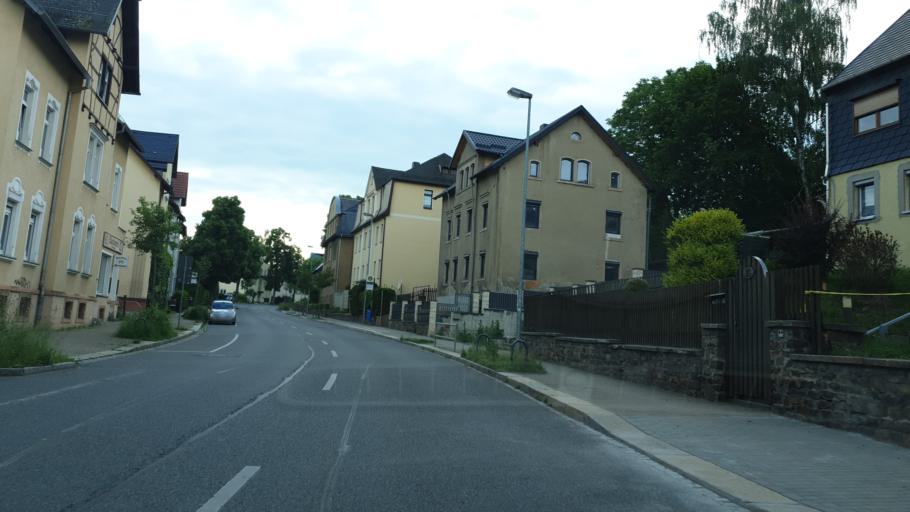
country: DE
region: Saxony
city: Neukirchen
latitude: 50.8128
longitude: 12.8234
